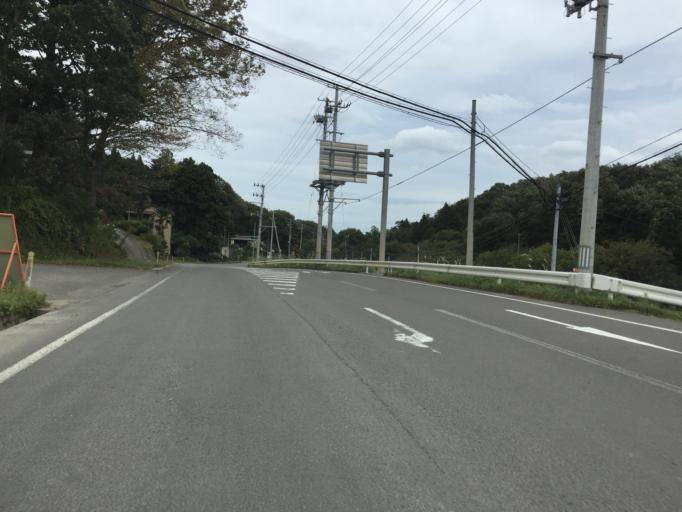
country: JP
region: Miyagi
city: Marumori
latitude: 37.8995
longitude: 140.7223
